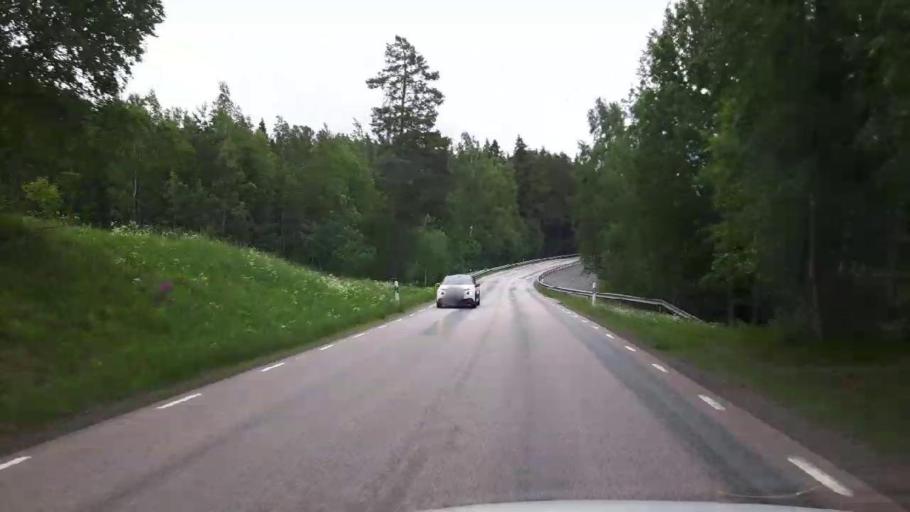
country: SE
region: Vaestmanland
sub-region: Kopings Kommun
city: Kolsva
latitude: 59.6334
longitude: 15.8004
